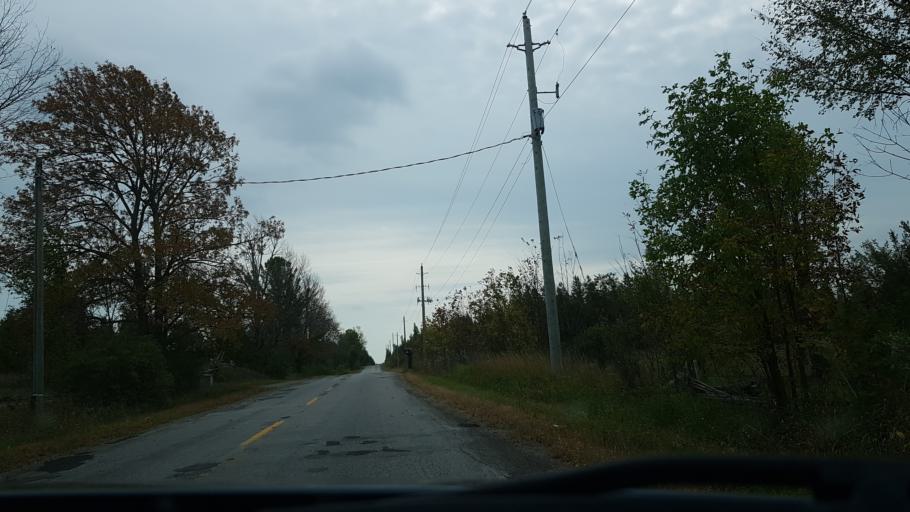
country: CA
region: Ontario
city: Orillia
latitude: 44.6478
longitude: -78.9637
